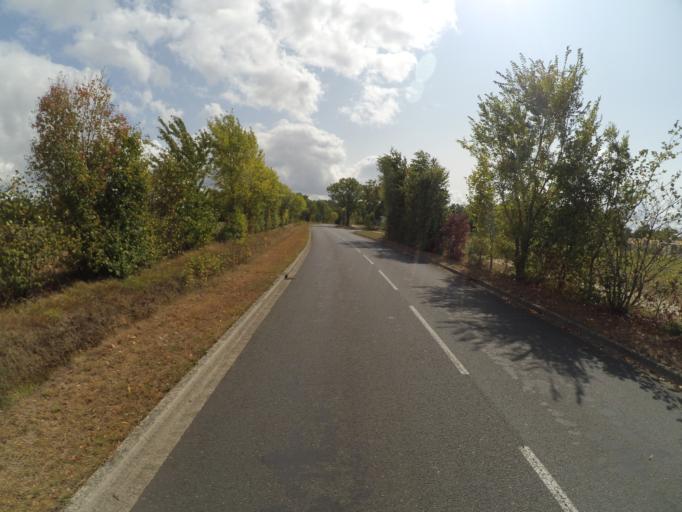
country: FR
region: Pays de la Loire
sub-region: Departement de la Vendee
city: Saint-Hilaire-de-Loulay
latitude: 47.0014
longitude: -1.3231
